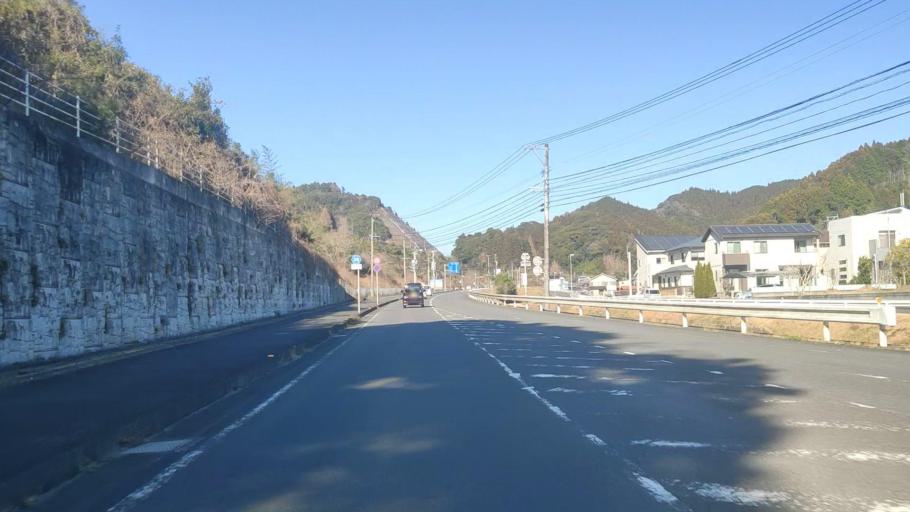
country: JP
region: Oita
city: Saiki
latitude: 32.9709
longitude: 131.8634
